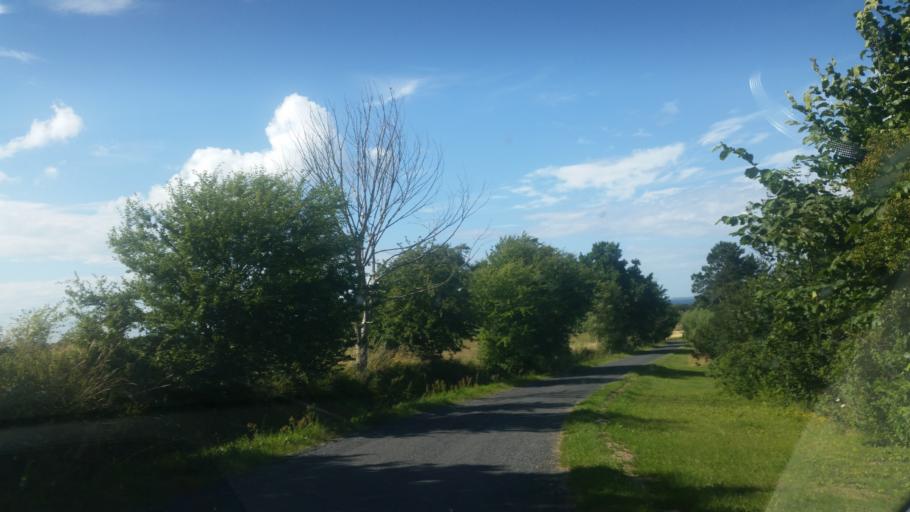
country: DK
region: Zealand
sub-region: Odsherred Kommune
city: Horve
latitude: 55.8124
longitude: 11.4036
